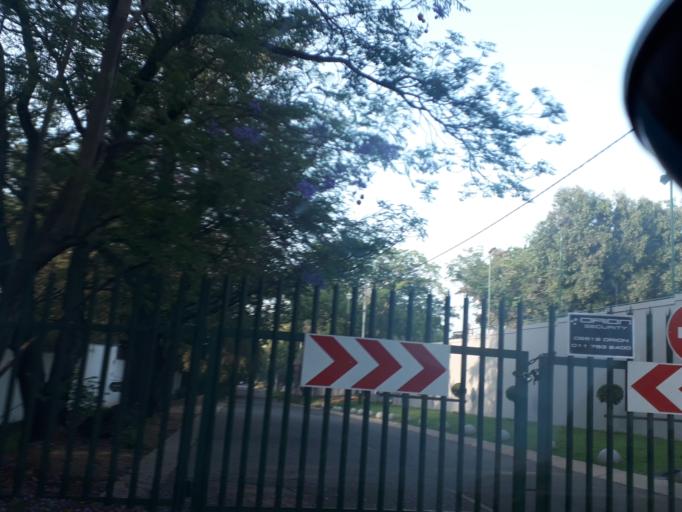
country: ZA
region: Gauteng
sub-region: City of Johannesburg Metropolitan Municipality
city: Midrand
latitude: -26.0657
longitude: 28.0320
